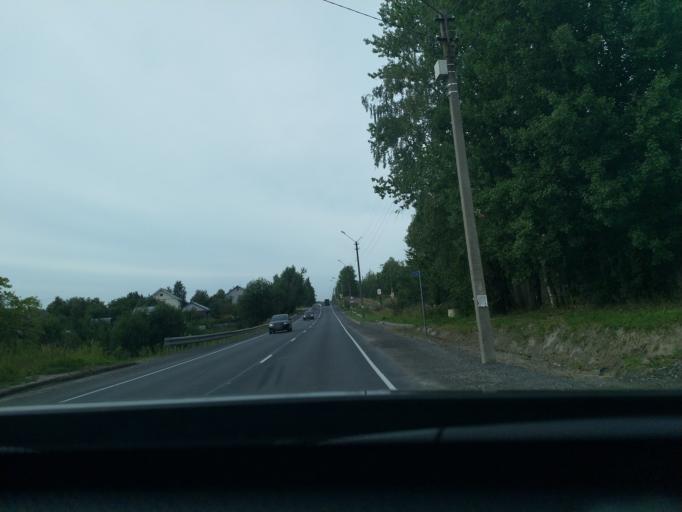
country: RU
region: Leningrad
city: Nikol'skoye
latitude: 59.7137
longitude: 30.7795
